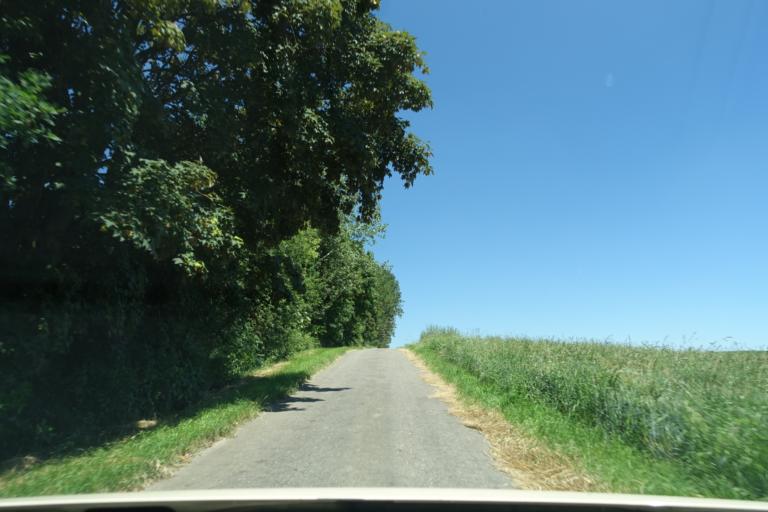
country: DE
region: Saxony
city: Eppendorf
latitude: 50.8097
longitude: 13.2315
